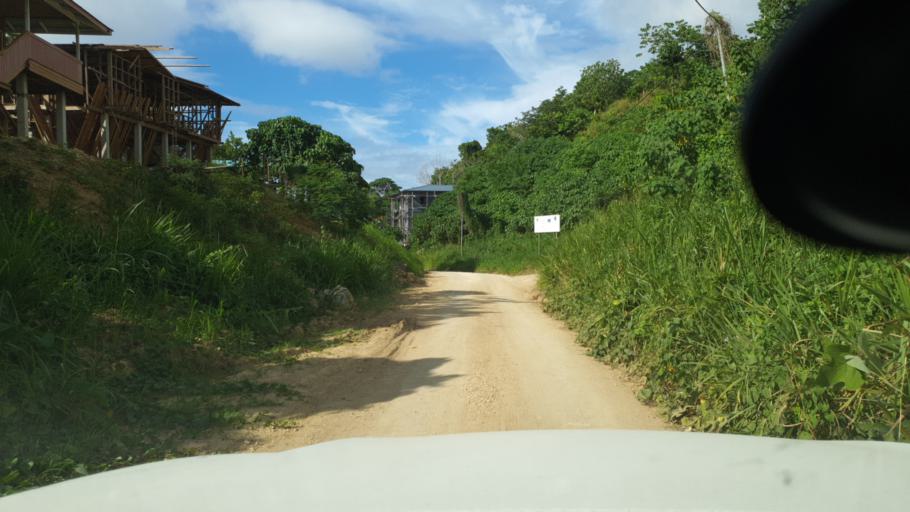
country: SB
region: Guadalcanal
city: Honiara
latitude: -9.4369
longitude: 159.9292
